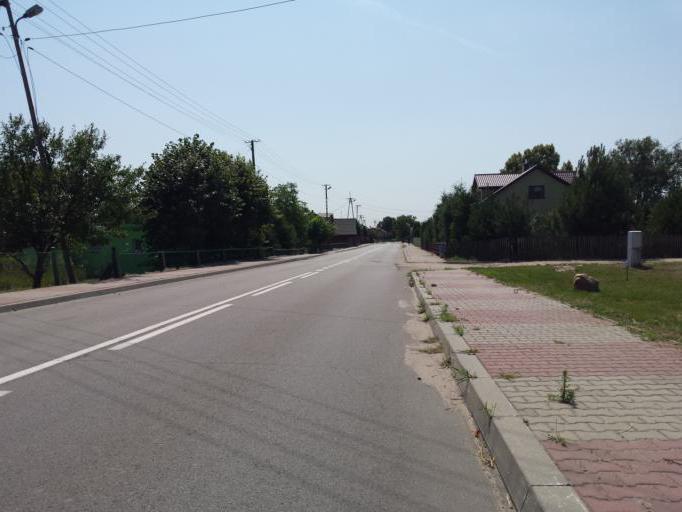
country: PL
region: Lublin Voivodeship
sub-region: Powiat bialski
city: Koden
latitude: 51.9039
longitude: 23.6012
